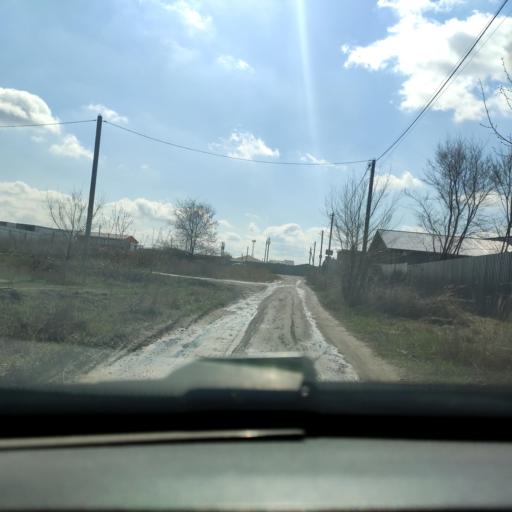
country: RU
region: Voronezj
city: Somovo
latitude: 51.6703
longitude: 39.3343
